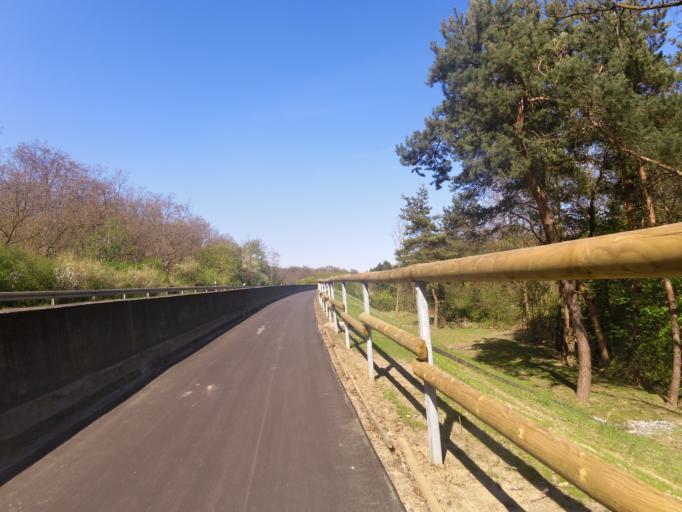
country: DE
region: Hesse
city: Morfelden-Walldorf
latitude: 50.0066
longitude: 8.5943
